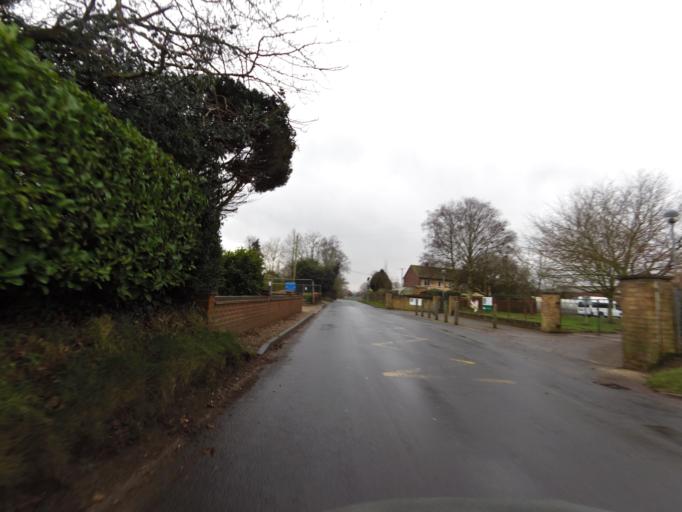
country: GB
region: England
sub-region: Norfolk
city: Briston
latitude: 52.7583
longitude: 1.1074
